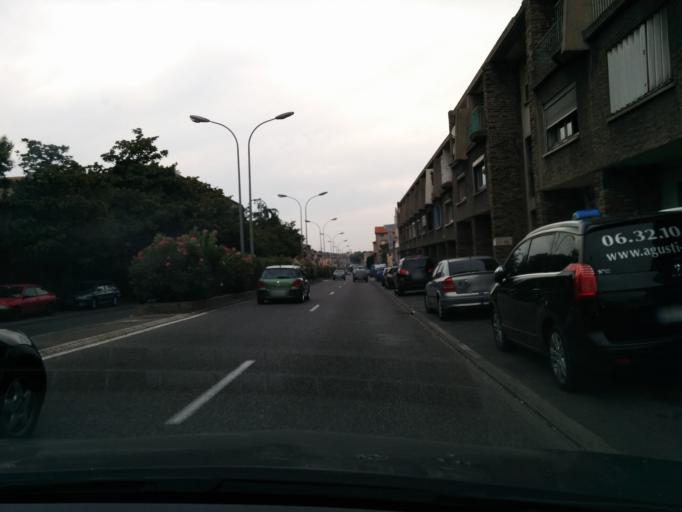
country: FR
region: Languedoc-Roussillon
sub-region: Departement de l'Aude
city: Carcassonne
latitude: 43.2095
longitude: 2.3672
